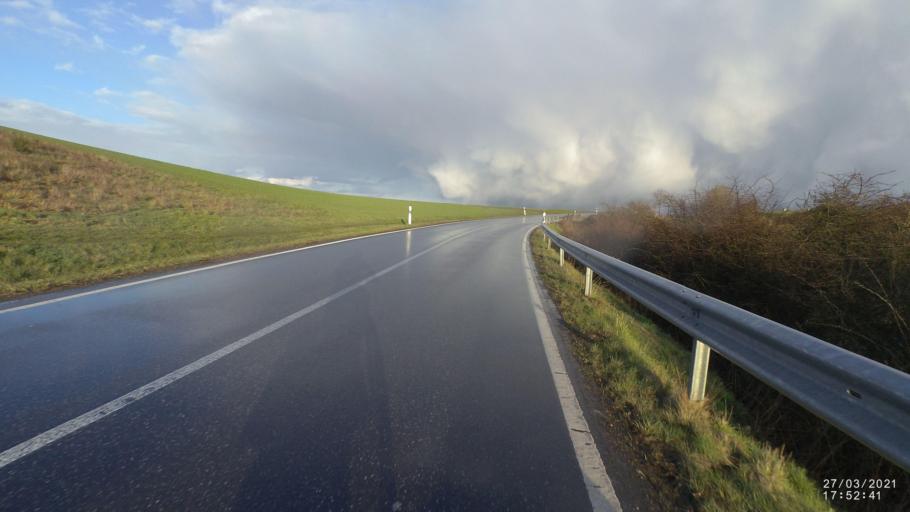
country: DE
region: Rheinland-Pfalz
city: Bell
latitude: 50.3839
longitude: 7.2429
